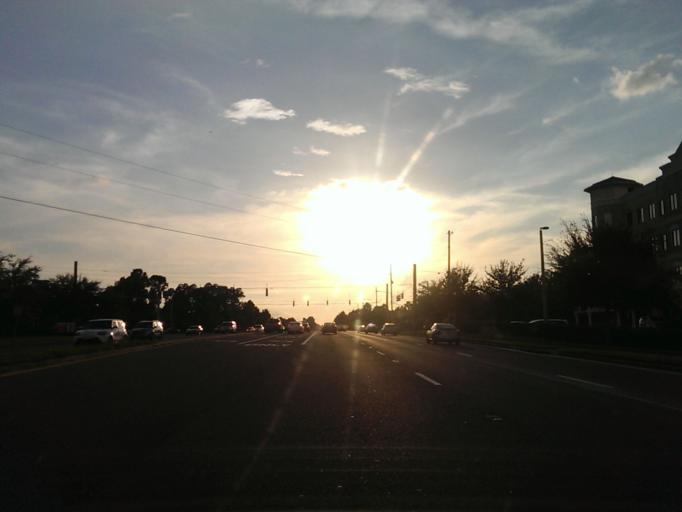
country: US
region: Florida
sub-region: Orange County
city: Orlovista
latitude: 28.4938
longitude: -81.4738
